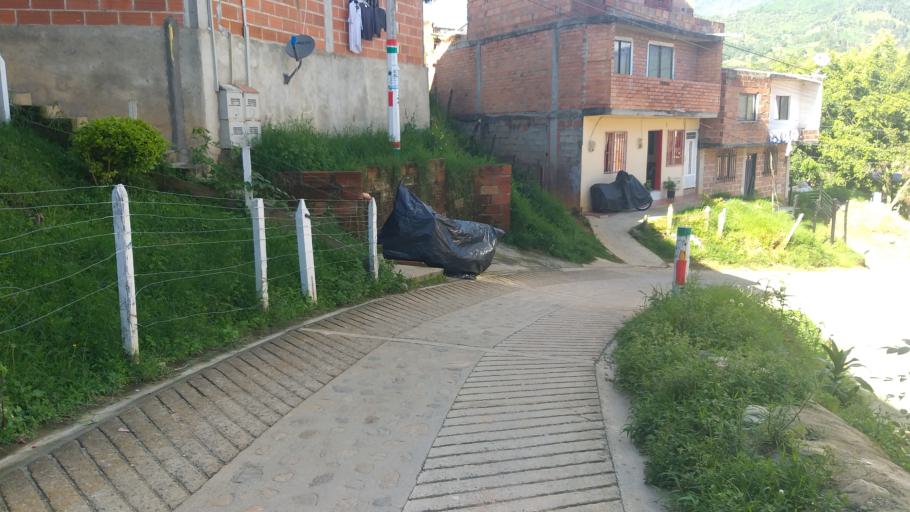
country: CO
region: Antioquia
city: Caldas
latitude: 6.0821
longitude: -75.6383
